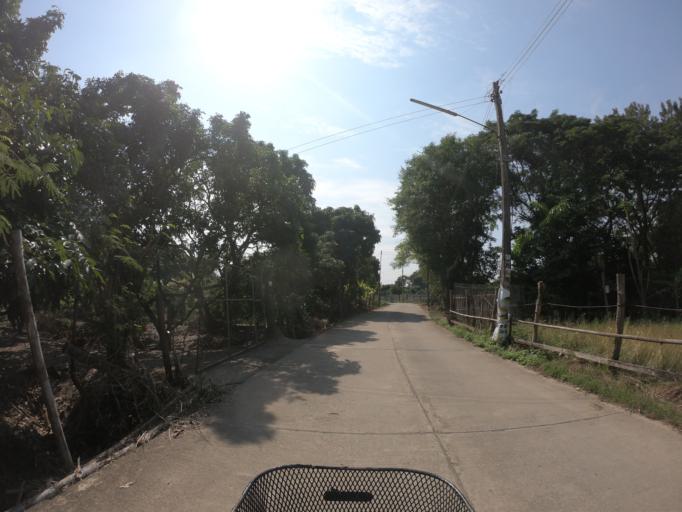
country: TH
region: Chiang Mai
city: Saraphi
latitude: 18.7119
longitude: 99.0493
